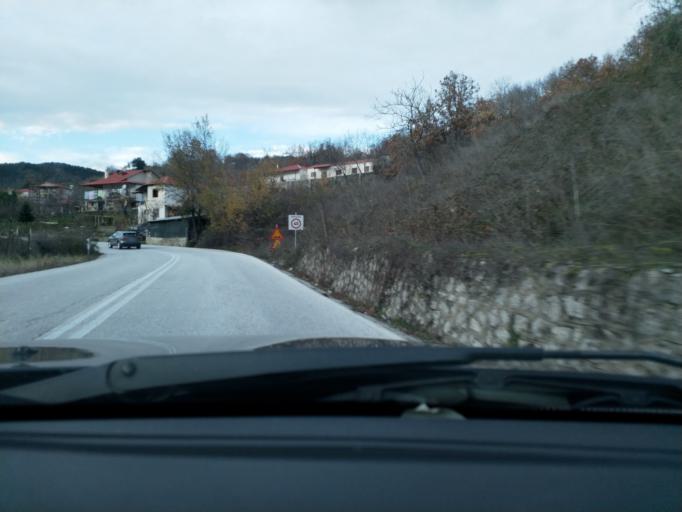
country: GR
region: Epirus
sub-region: Nomos Ioanninon
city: Metsovo
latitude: 39.8080
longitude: 21.3481
